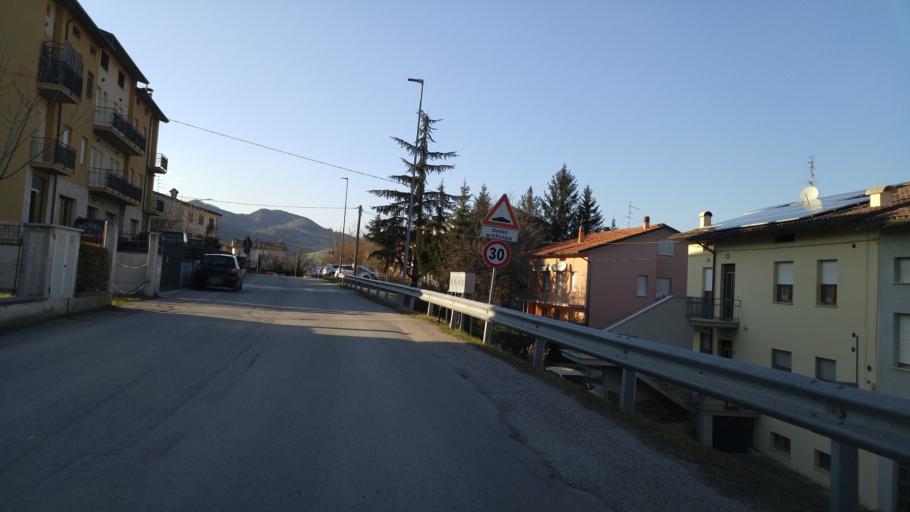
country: IT
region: The Marches
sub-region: Provincia di Pesaro e Urbino
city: Cagli
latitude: 43.5469
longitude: 12.6592
